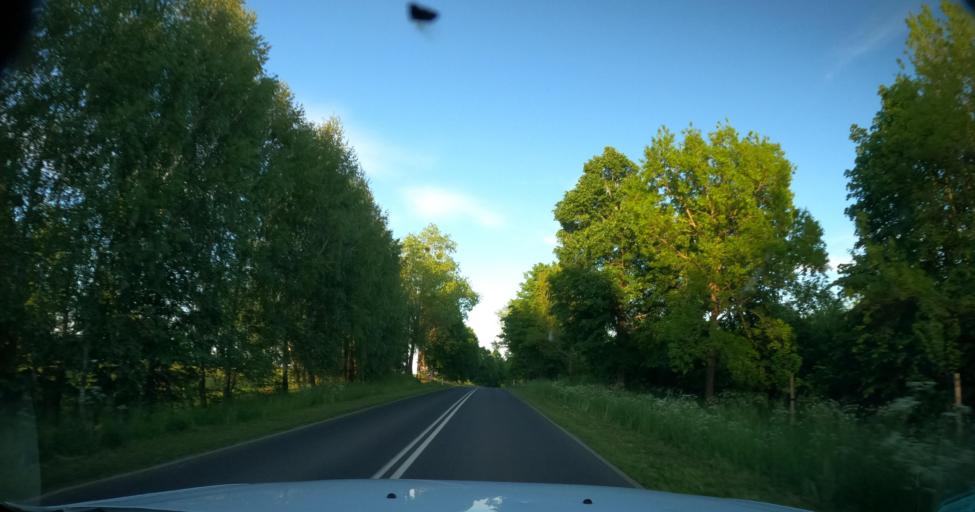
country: PL
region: Warmian-Masurian Voivodeship
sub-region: Powiat lidzbarski
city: Lidzbark Warminski
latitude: 54.1446
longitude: 20.4957
